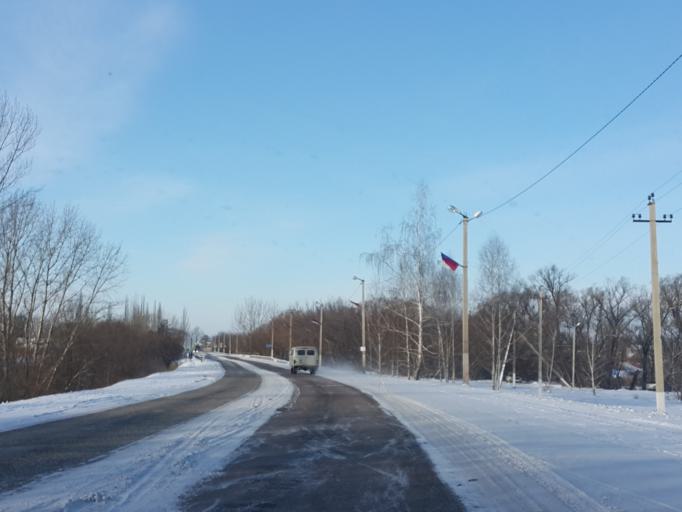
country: RU
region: Tambov
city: Znamenka
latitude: 52.4173
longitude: 41.4372
